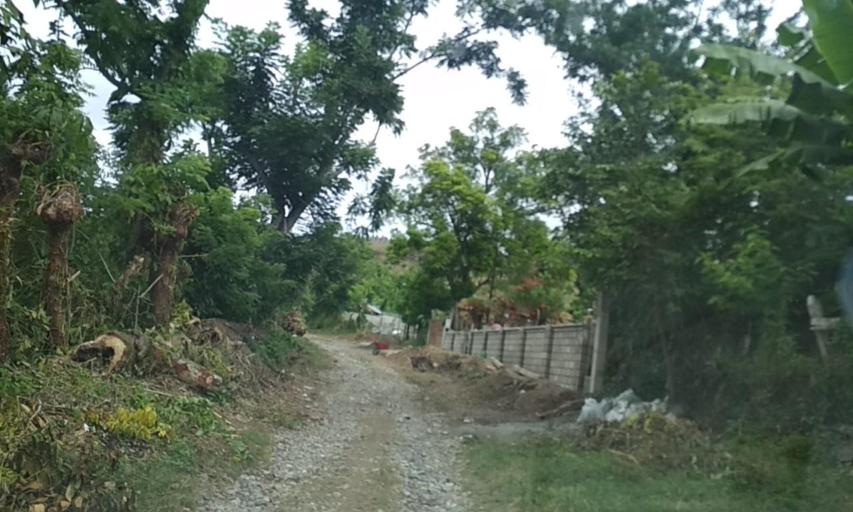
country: MX
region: Veracruz
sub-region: Papantla
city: Residencial Tajin
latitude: 20.6040
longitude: -97.3349
